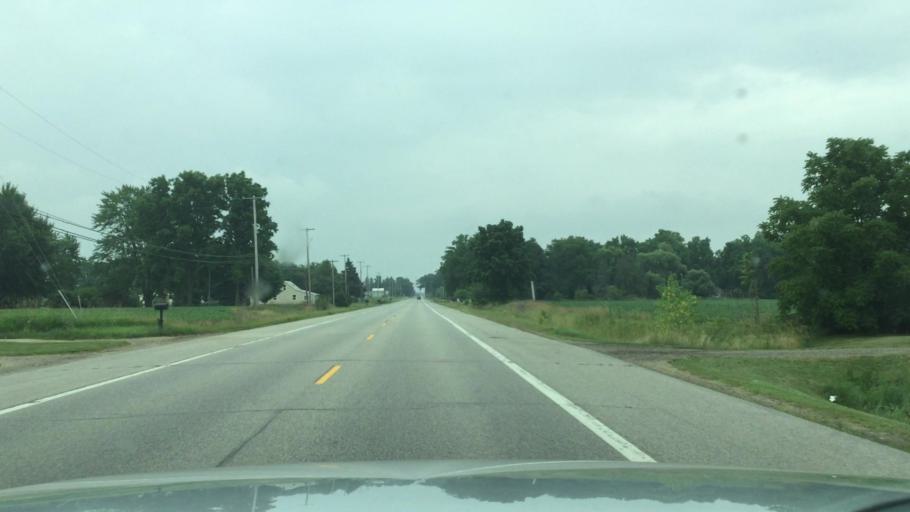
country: US
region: Michigan
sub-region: Shiawassee County
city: New Haven
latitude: 43.0491
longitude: -84.1771
